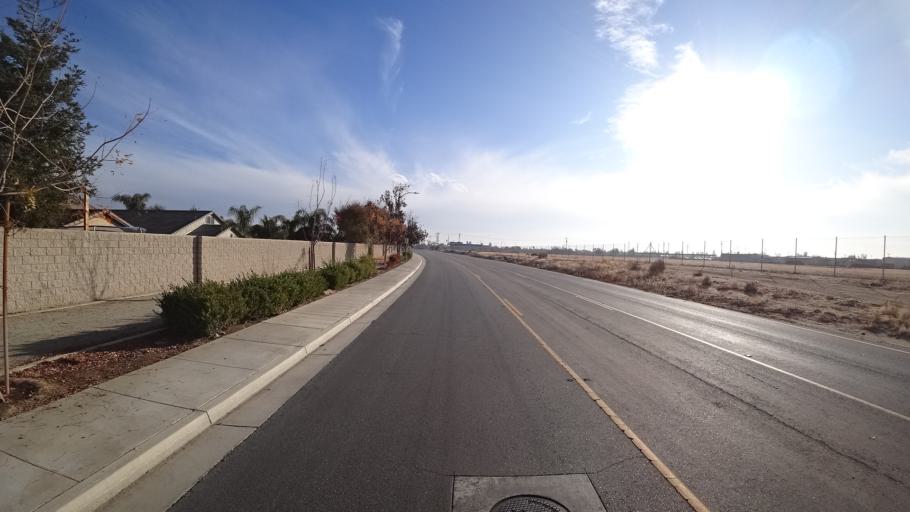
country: US
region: California
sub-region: Kern County
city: Rosedale
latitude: 35.4054
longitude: -119.1482
